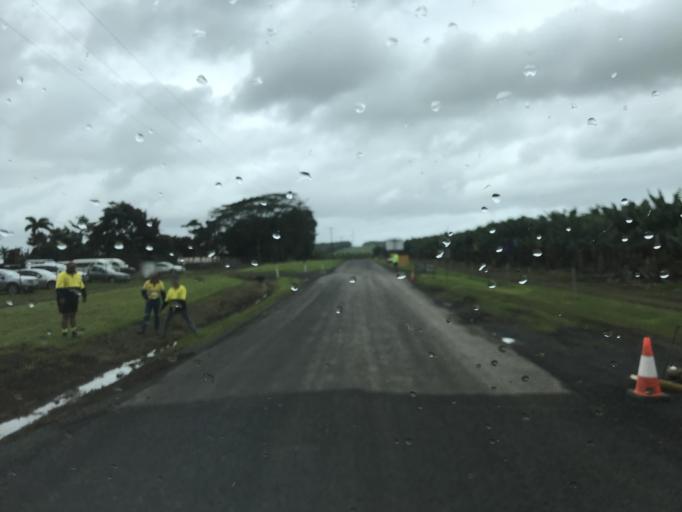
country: AU
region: Queensland
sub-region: Cassowary Coast
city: Innisfail
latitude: -17.5020
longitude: 145.9819
